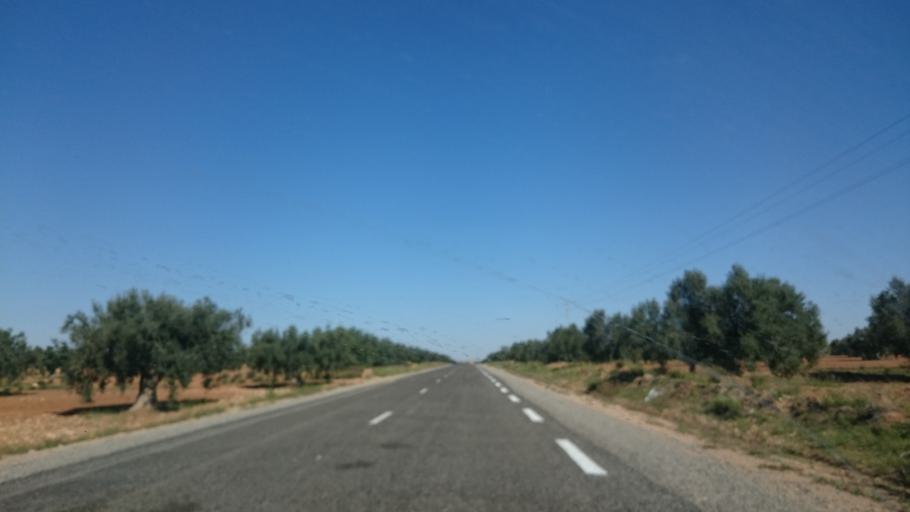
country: TN
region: Safaqis
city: Sfax
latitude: 34.8479
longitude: 10.4499
